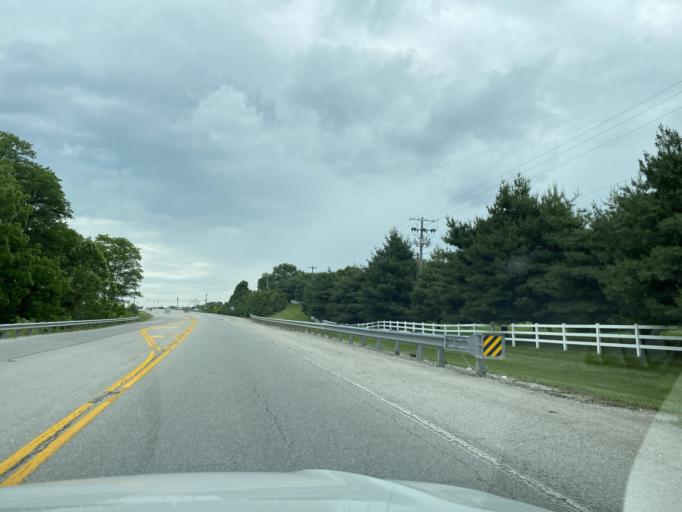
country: US
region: Kentucky
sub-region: Scott County
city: Georgetown
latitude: 38.2173
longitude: -84.5284
